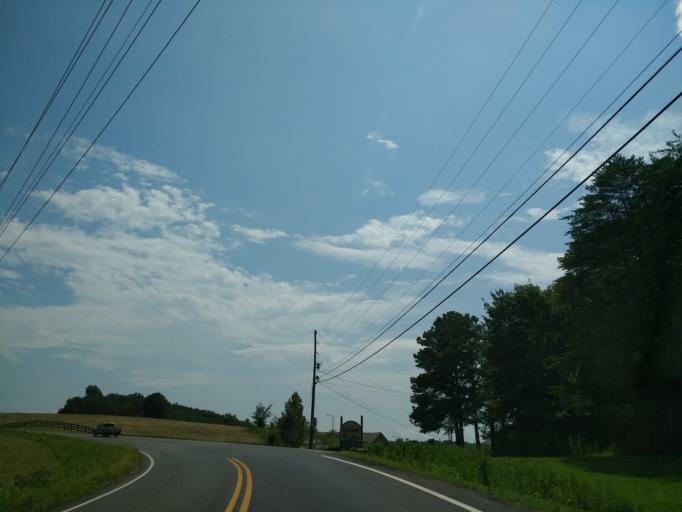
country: US
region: Georgia
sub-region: White County
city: Cleveland
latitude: 34.6550
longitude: -83.7960
